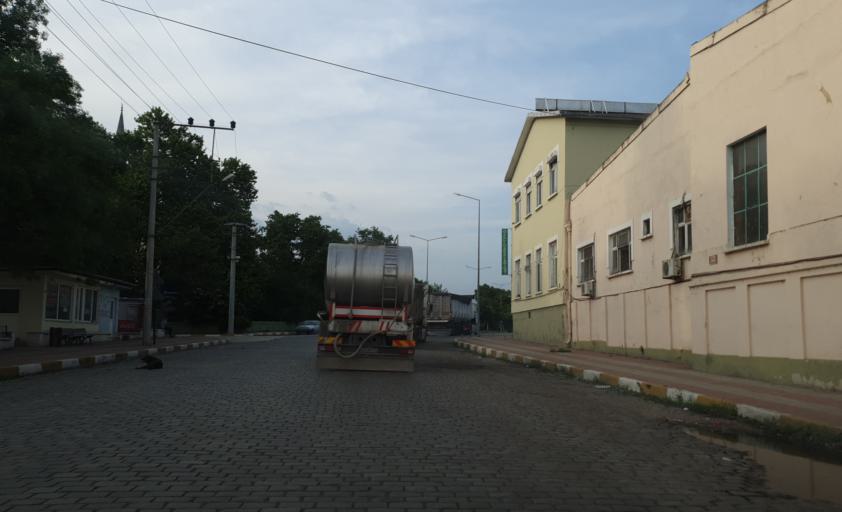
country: TR
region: Kirklareli
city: Babaeski
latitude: 41.3668
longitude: 27.1428
